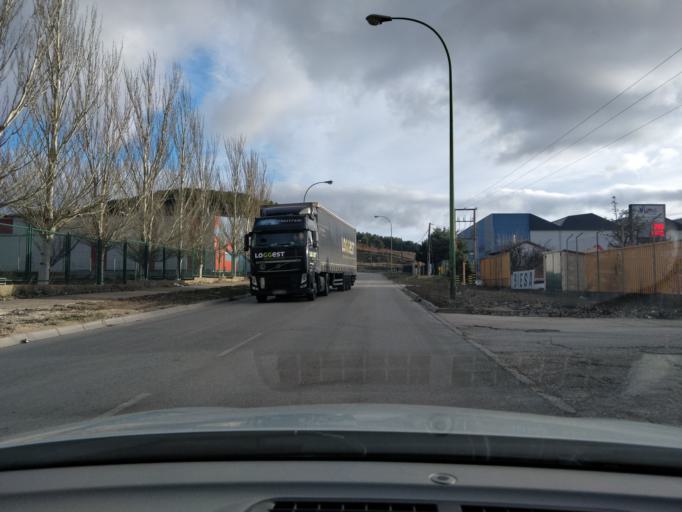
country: ES
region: Castille and Leon
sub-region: Provincia de Burgos
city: Villalbilla de Burgos
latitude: 42.3646
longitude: -3.7523
